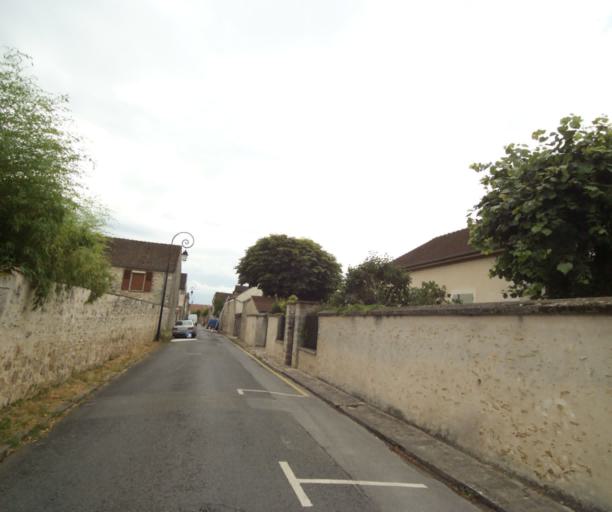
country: FR
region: Ile-de-France
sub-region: Departement de l'Essonne
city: Soisy-sur-Ecole
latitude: 48.4785
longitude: 2.4927
